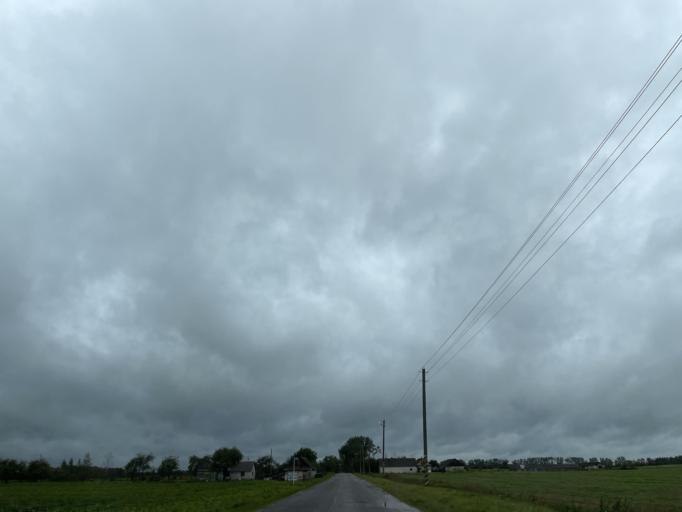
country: BY
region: Brest
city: Lyakhavichy
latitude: 53.1922
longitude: 26.2484
